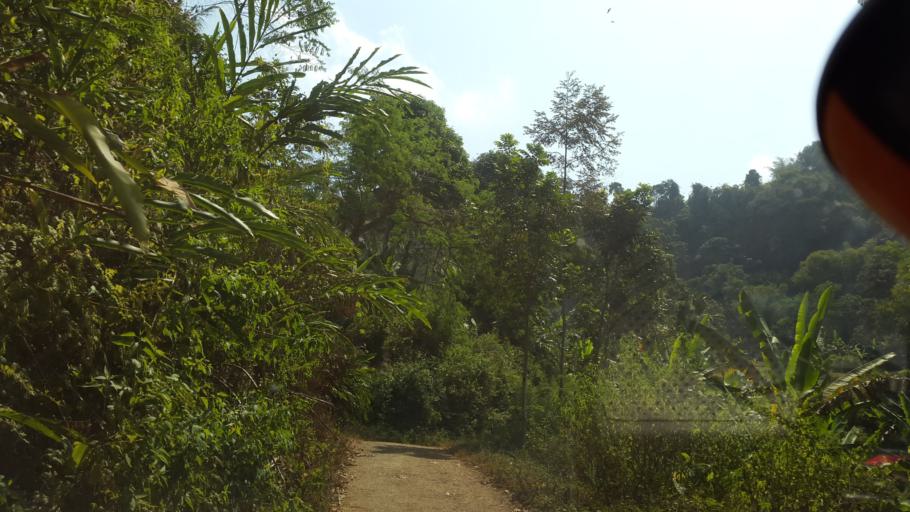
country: ID
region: West Java
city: Babakan
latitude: -7.2196
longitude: 106.7833
